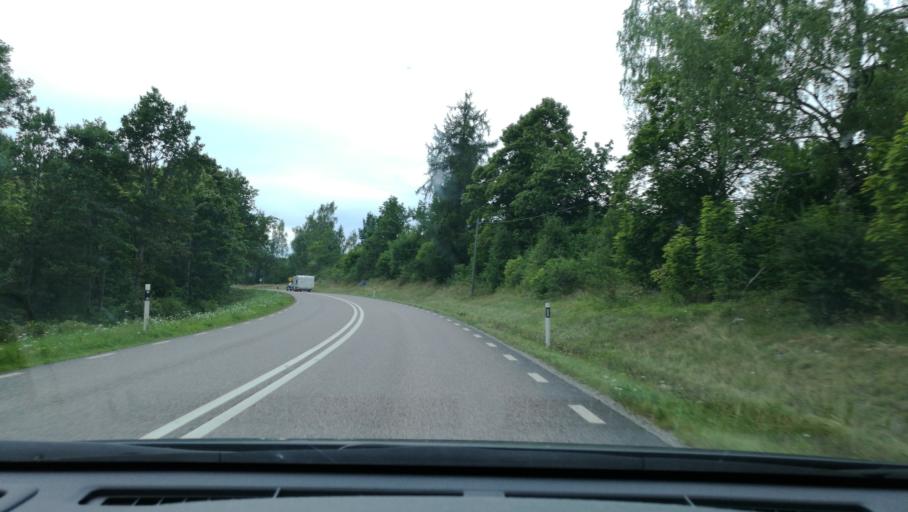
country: SE
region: Soedermanland
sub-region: Katrineholms Kommun
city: Katrineholm
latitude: 59.1481
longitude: 16.1175
